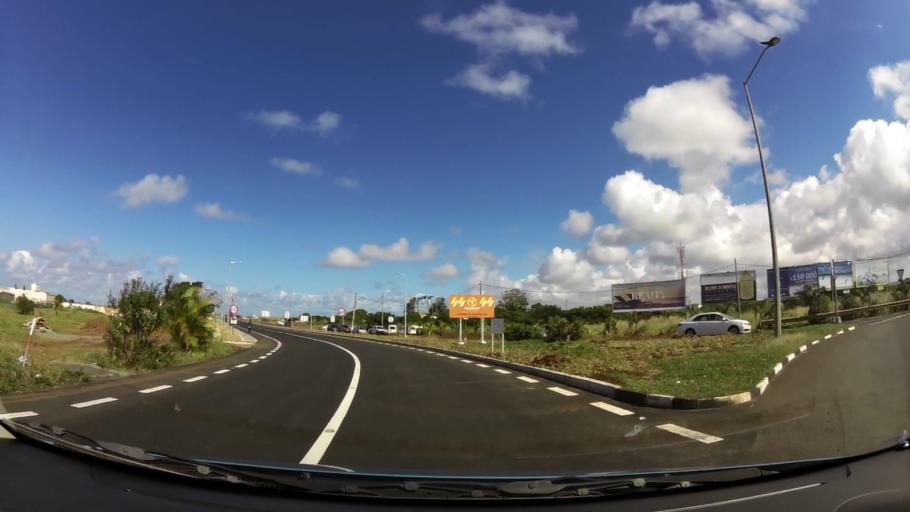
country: MU
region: Grand Port
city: Plaine Magnien
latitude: -20.4349
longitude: 57.6740
